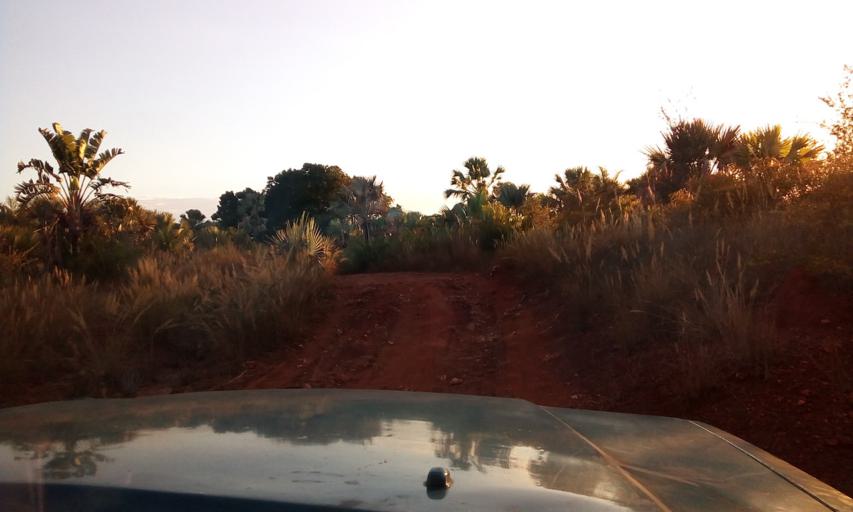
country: MG
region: Boeny
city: Sitampiky
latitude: -16.1253
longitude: 45.4333
